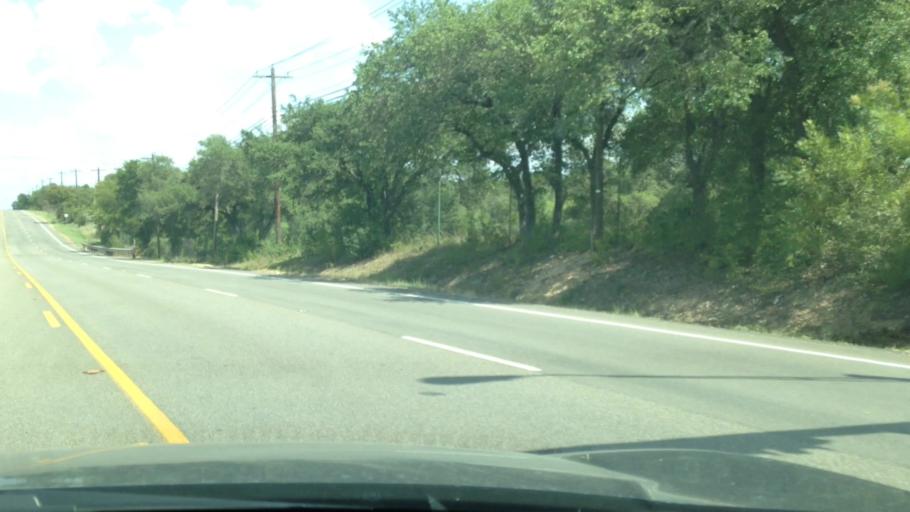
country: US
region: Texas
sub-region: Williamson County
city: Leander
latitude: 30.6364
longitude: -97.7928
